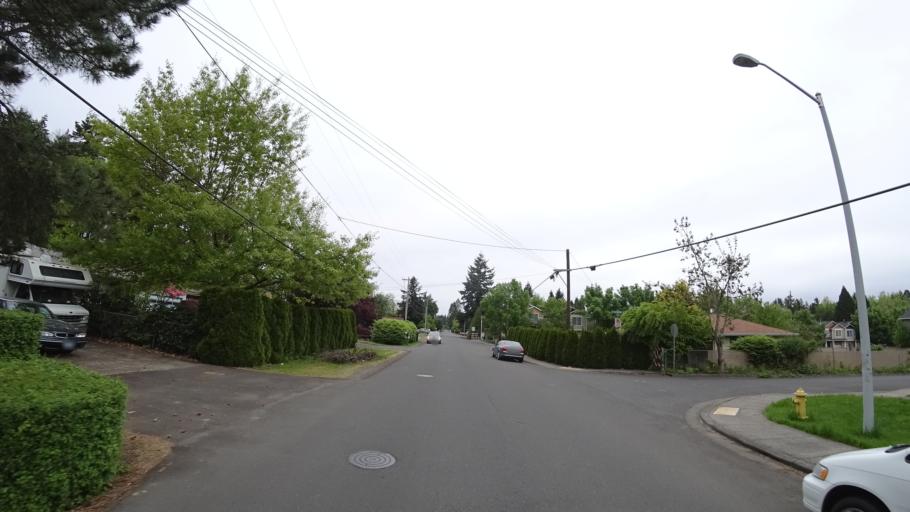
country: US
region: Oregon
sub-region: Washington County
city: Aloha
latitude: 45.5020
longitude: -122.8752
